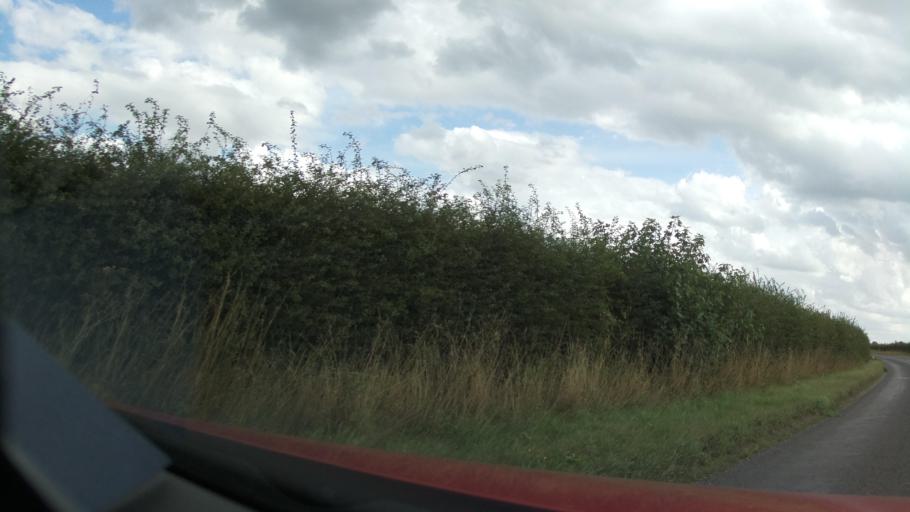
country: GB
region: England
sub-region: North Yorkshire
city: Ripon
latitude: 54.1665
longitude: -1.5498
